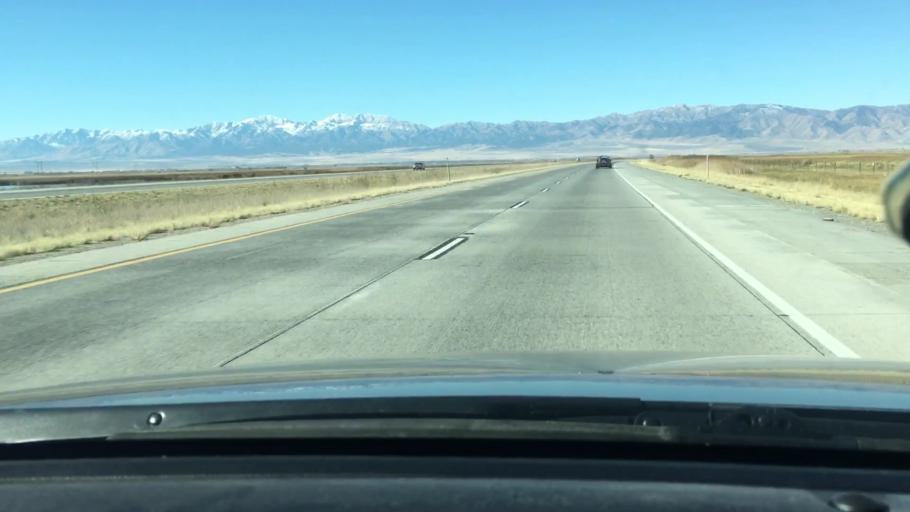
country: US
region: Utah
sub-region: Tooele County
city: Stansbury park
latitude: 40.6669
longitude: -112.3081
